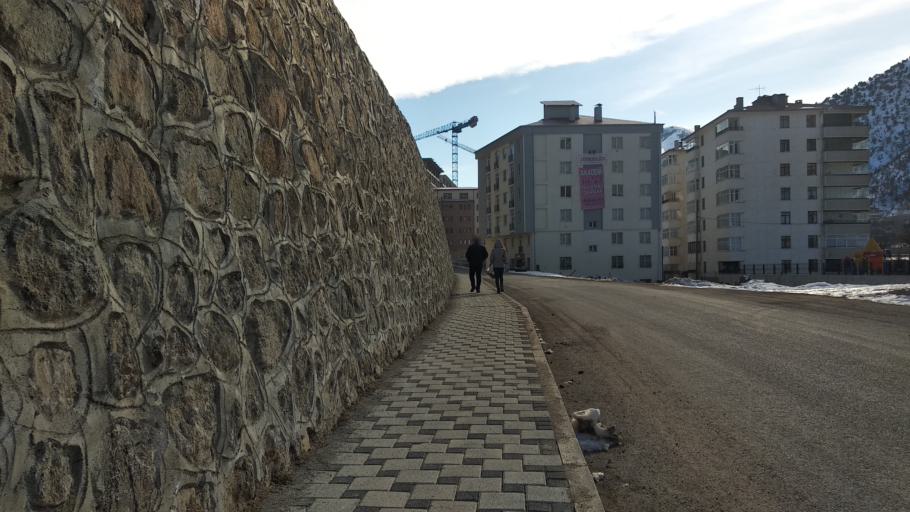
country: TR
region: Gumushane
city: Gumushkhane
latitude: 40.4397
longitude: 39.5043
